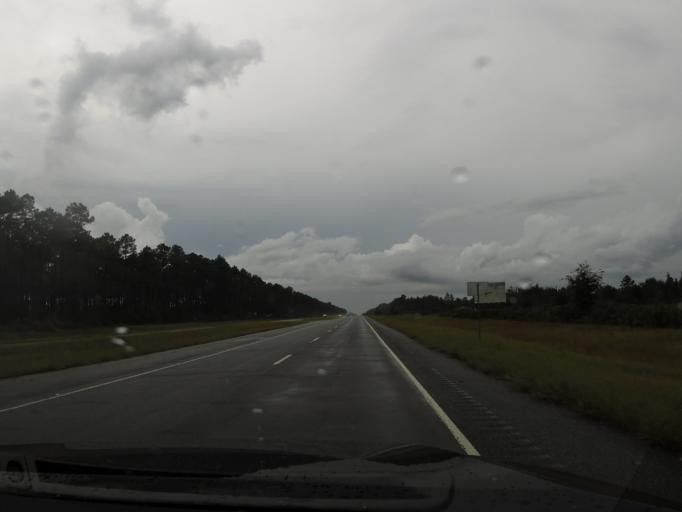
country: US
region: Georgia
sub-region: Wayne County
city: Jesup
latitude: 31.4756
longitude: -81.7265
